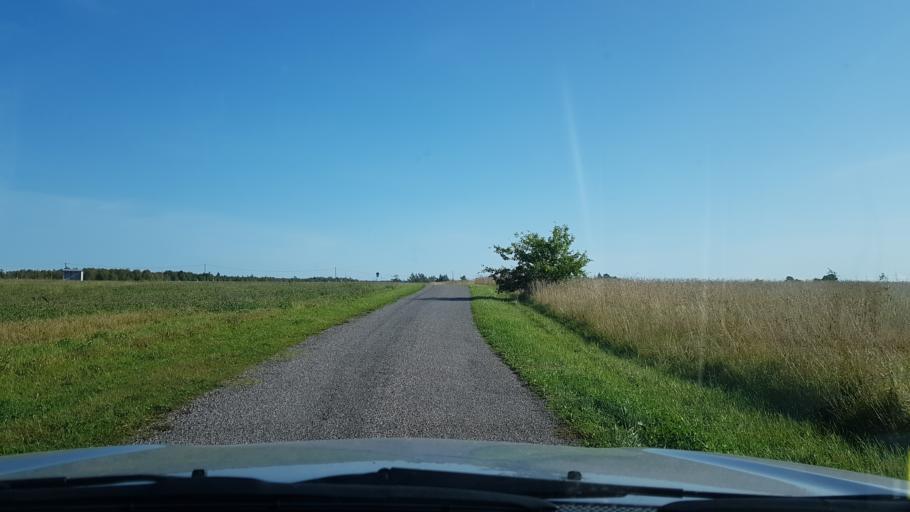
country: EE
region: Ida-Virumaa
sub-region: Narva-Joesuu linn
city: Narva-Joesuu
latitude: 59.3998
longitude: 28.0052
